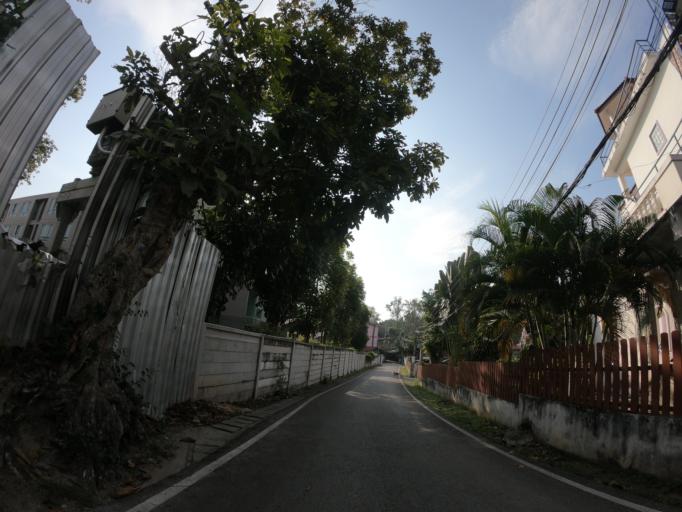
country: TH
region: Chiang Mai
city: Chiang Mai
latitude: 18.7928
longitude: 98.9484
